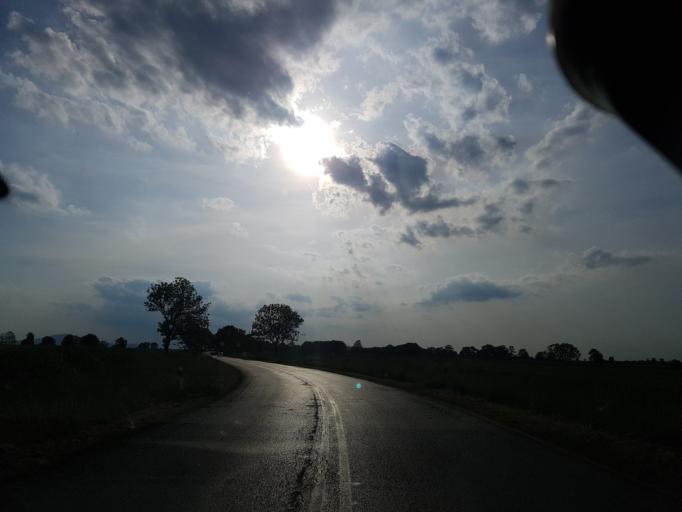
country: PL
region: Lower Silesian Voivodeship
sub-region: Powiat wroclawski
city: Kobierzyce
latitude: 50.9158
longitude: 16.9879
